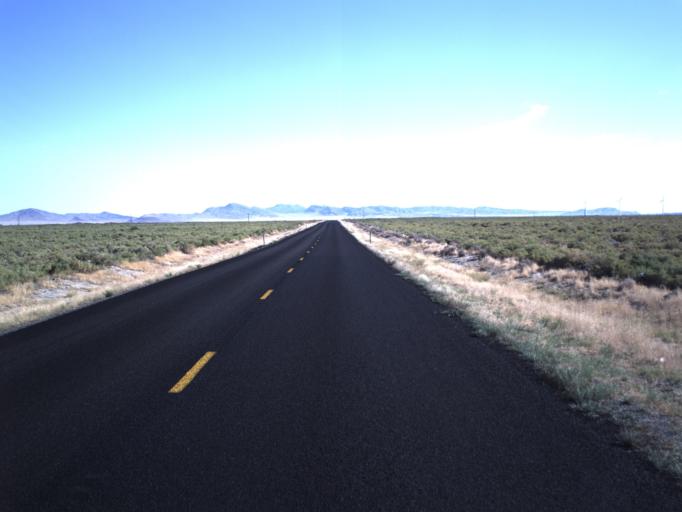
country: US
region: Utah
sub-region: Beaver County
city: Milford
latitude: 38.5476
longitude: -112.9912
